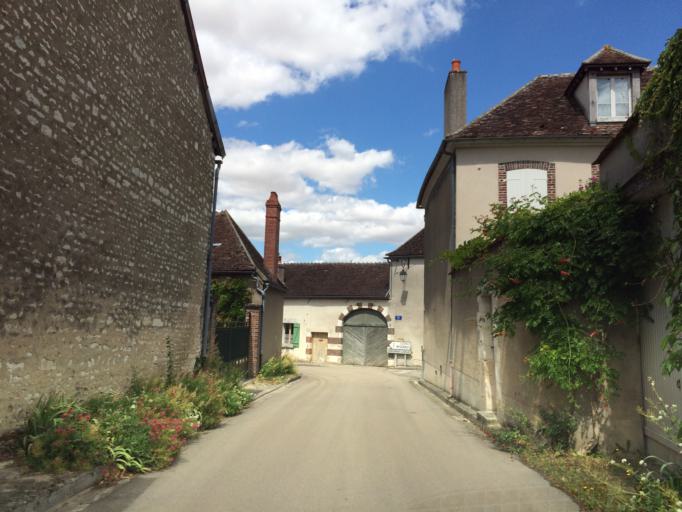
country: FR
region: Bourgogne
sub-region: Departement de l'Yonne
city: Fleury-la-Vallee
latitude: 47.9129
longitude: 3.4755
